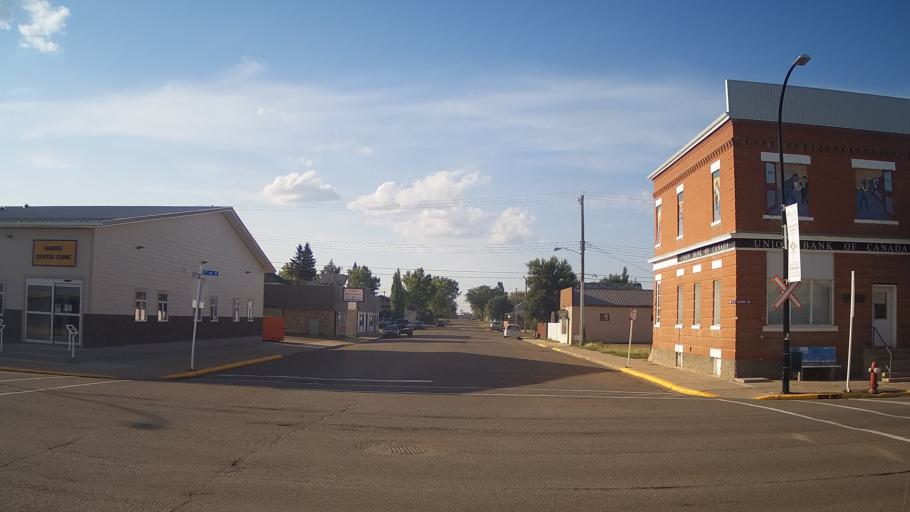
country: CA
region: Alberta
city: Hanna
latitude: 51.6423
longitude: -111.9292
